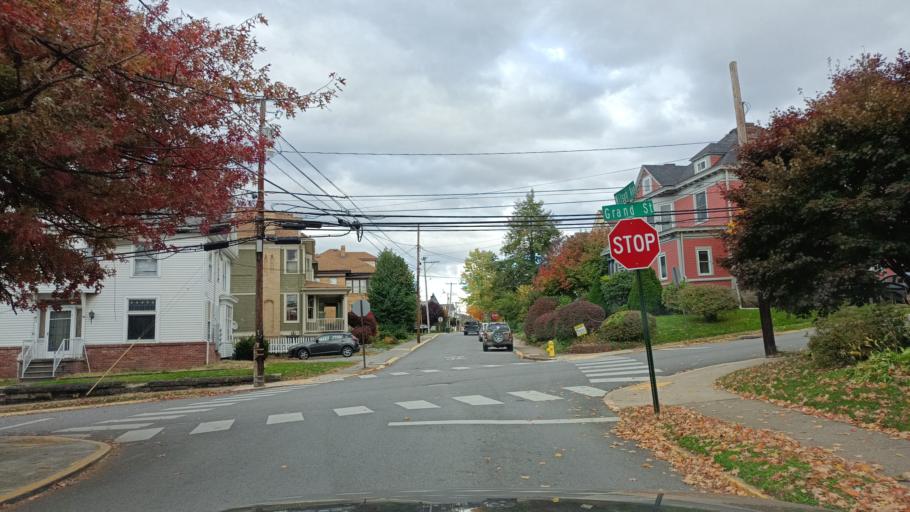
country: US
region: West Virginia
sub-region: Monongalia County
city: Morgantown
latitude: 39.6235
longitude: -79.9549
